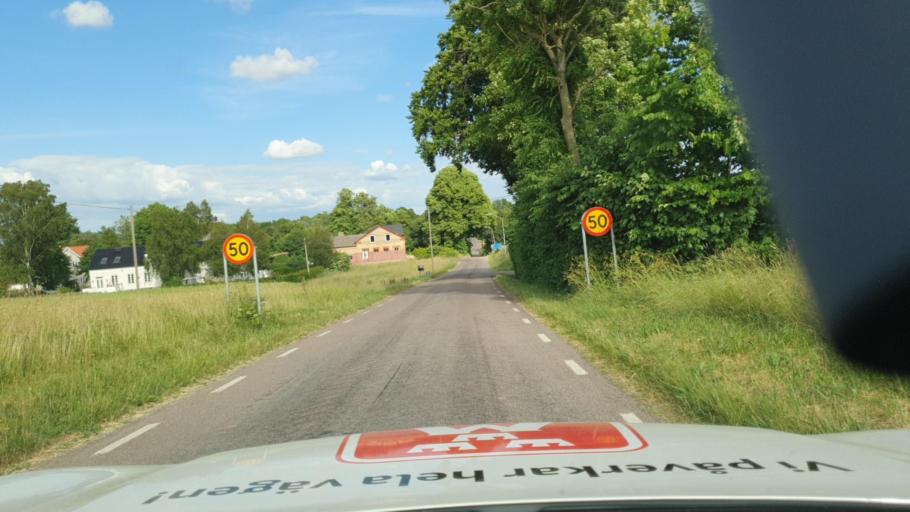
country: SE
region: Skane
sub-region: Skurups Kommun
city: Rydsgard
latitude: 55.4496
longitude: 13.5880
